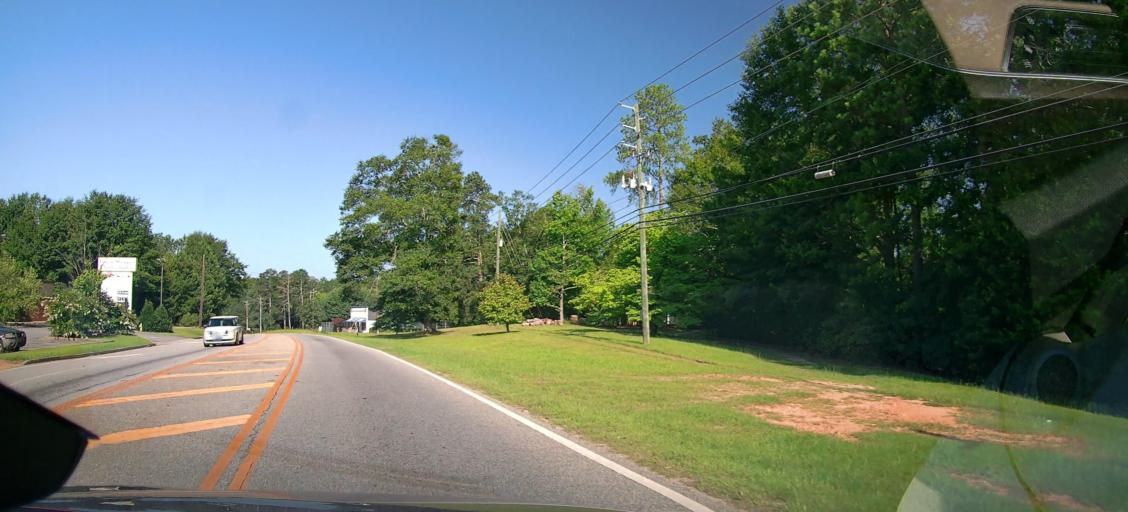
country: US
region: Georgia
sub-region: Peach County
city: Byron
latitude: 32.7448
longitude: -83.7055
